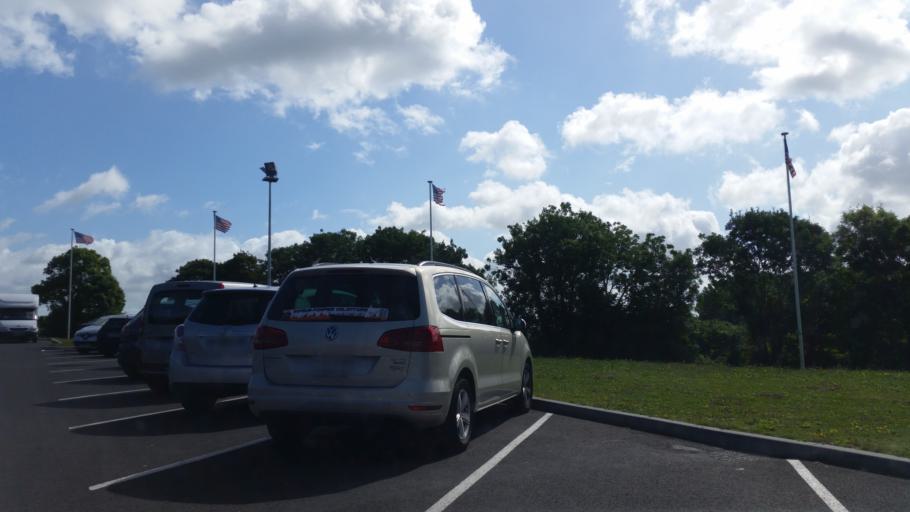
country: FR
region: Lower Normandy
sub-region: Departement de la Manche
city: Carentan
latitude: 49.3295
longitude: -1.2682
